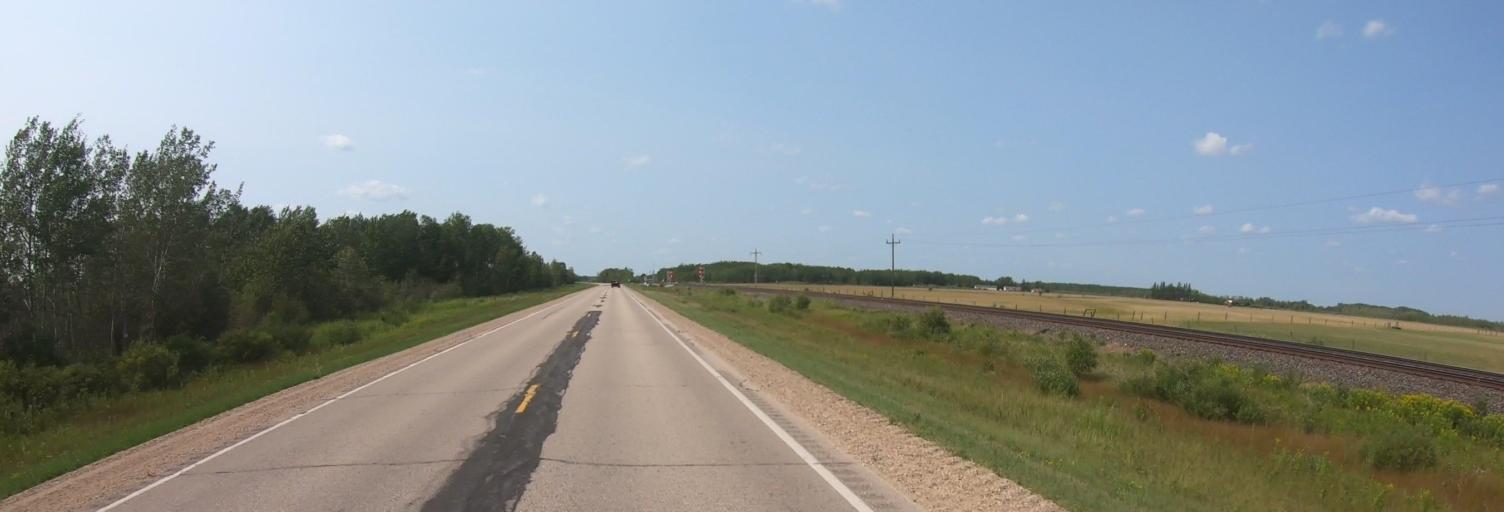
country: US
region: Minnesota
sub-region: Lake of the Woods County
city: Baudette
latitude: 48.7363
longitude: -94.8206
